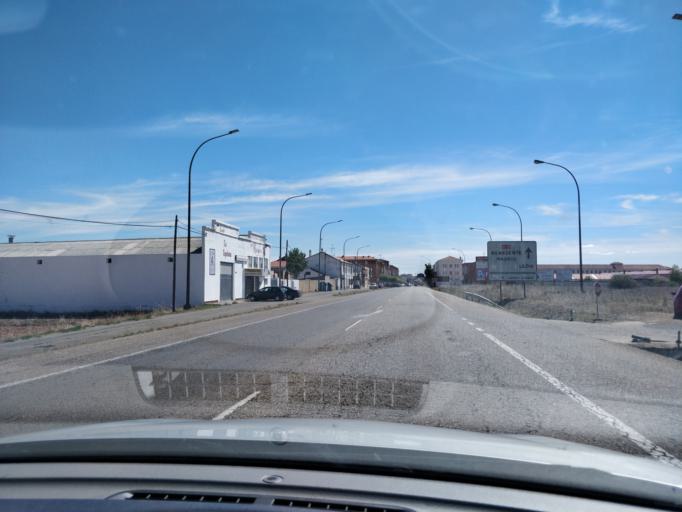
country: ES
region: Castille and Leon
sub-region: Provincia de Leon
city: Astorga
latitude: 42.4640
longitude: -6.0718
